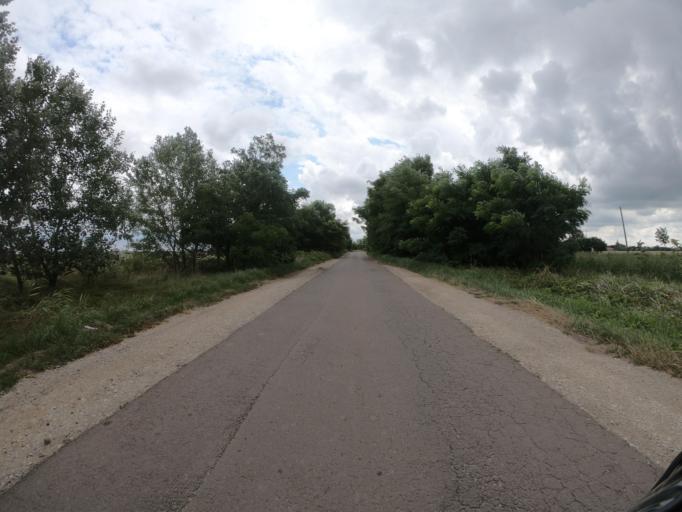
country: HU
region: Borsod-Abauj-Zemplen
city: Szentistvan
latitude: 47.7084
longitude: 20.7000
